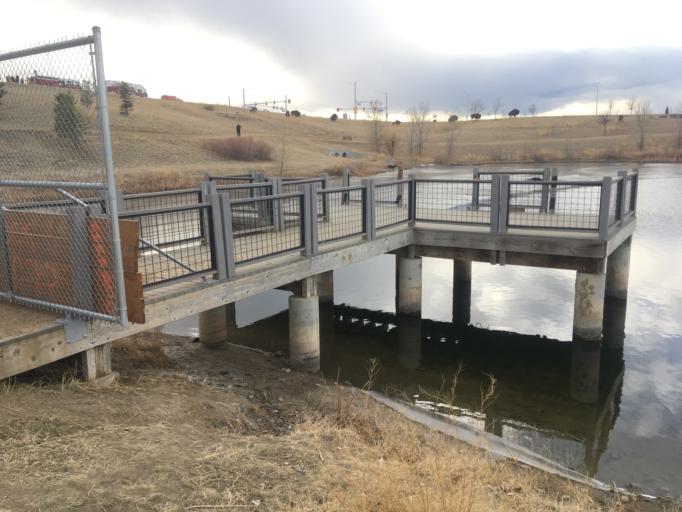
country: US
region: Colorado
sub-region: Boulder County
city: Lafayette
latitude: 39.9795
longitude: -105.0324
